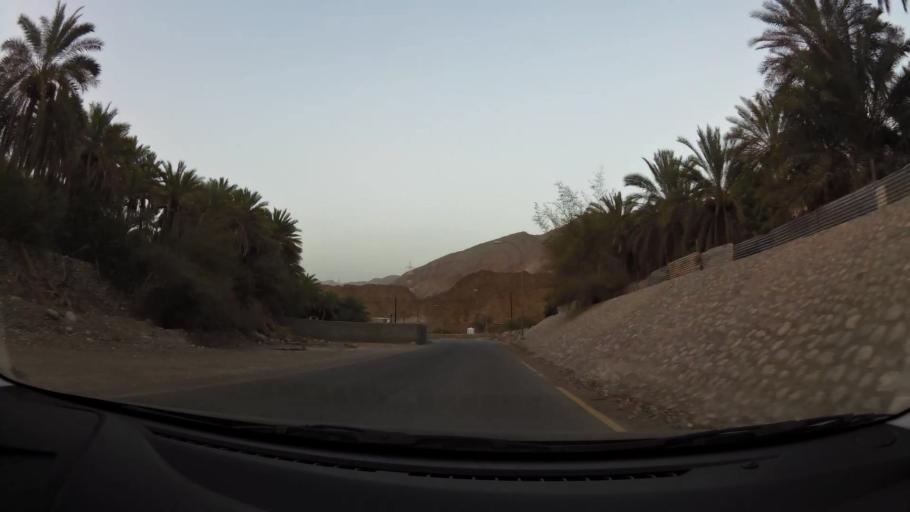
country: OM
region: Muhafazat Masqat
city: Bawshar
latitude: 23.4777
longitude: 58.3287
